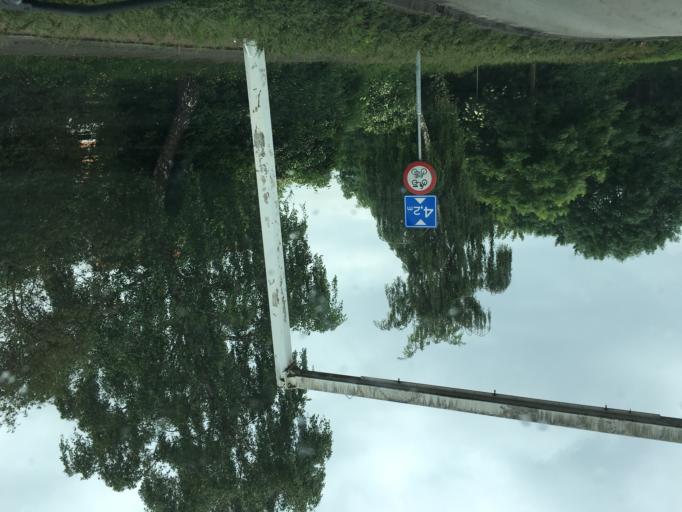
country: NL
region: South Holland
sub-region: Gemeente Capelle aan den IJssel
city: Capelle aan den IJssel
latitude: 51.9550
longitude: 4.5868
